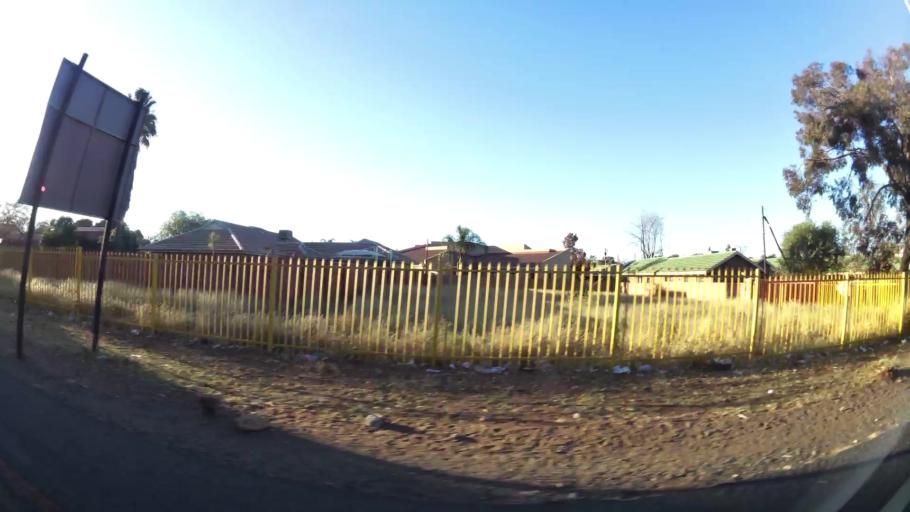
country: ZA
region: Northern Cape
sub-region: Frances Baard District Municipality
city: Kimberley
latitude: -28.7631
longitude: 24.7576
